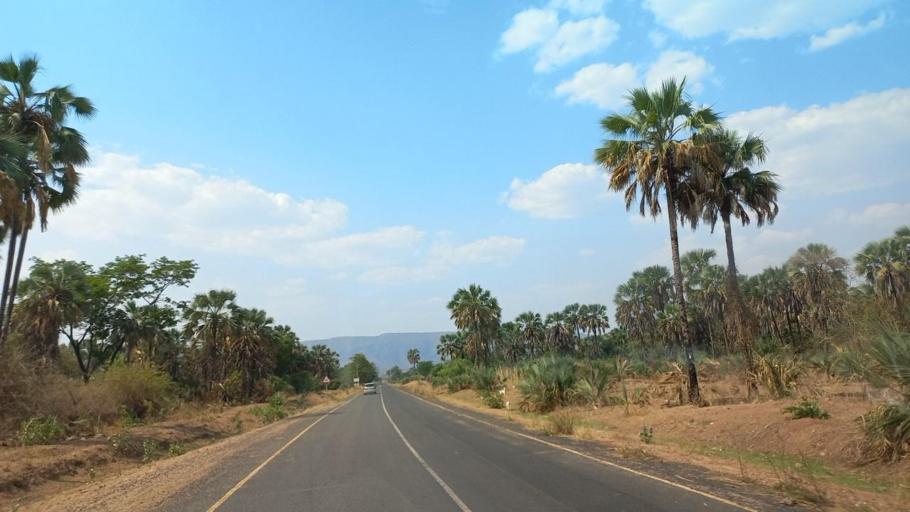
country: ZM
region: Lusaka
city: Luangwa
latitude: -15.0907
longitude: 30.1926
